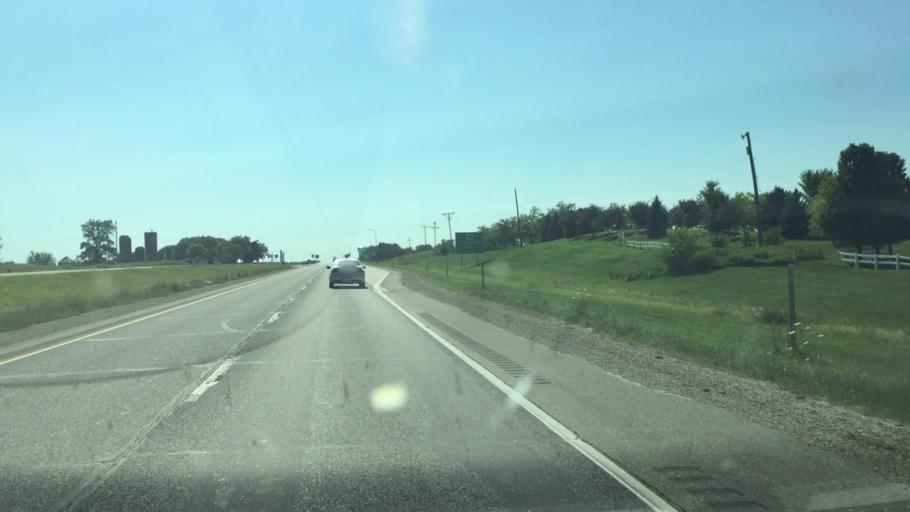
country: US
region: Iowa
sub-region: Linn County
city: Ely
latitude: 41.9264
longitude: -91.6150
